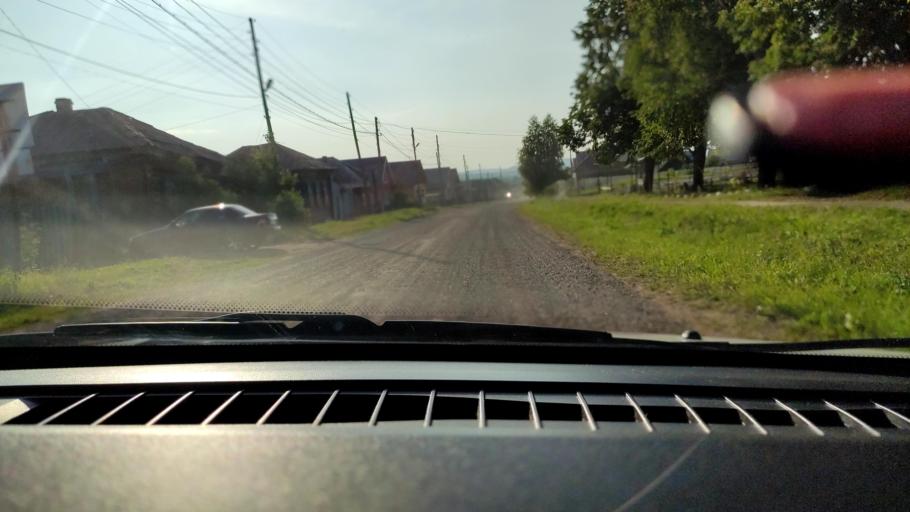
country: RU
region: Perm
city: Zvezdnyy
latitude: 57.7922
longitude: 56.3212
